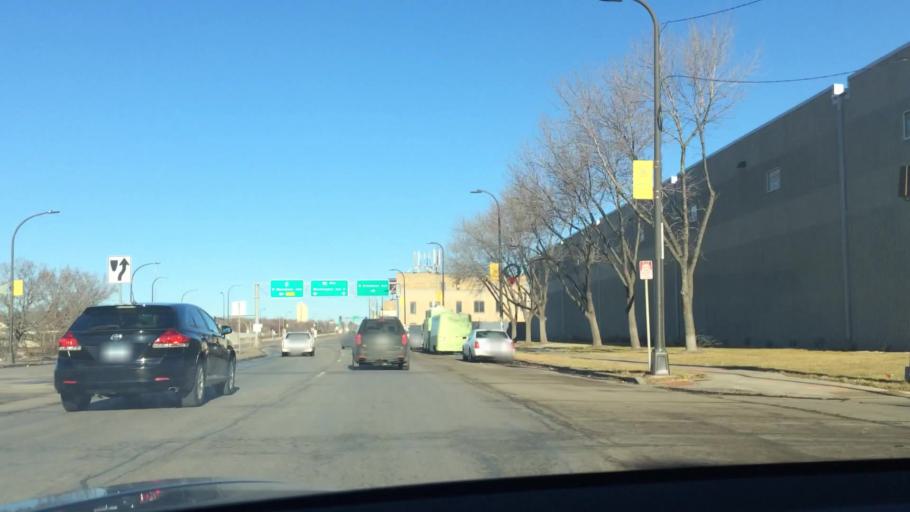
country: US
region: Minnesota
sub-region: Hennepin County
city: Minneapolis
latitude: 44.9974
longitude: -93.2815
